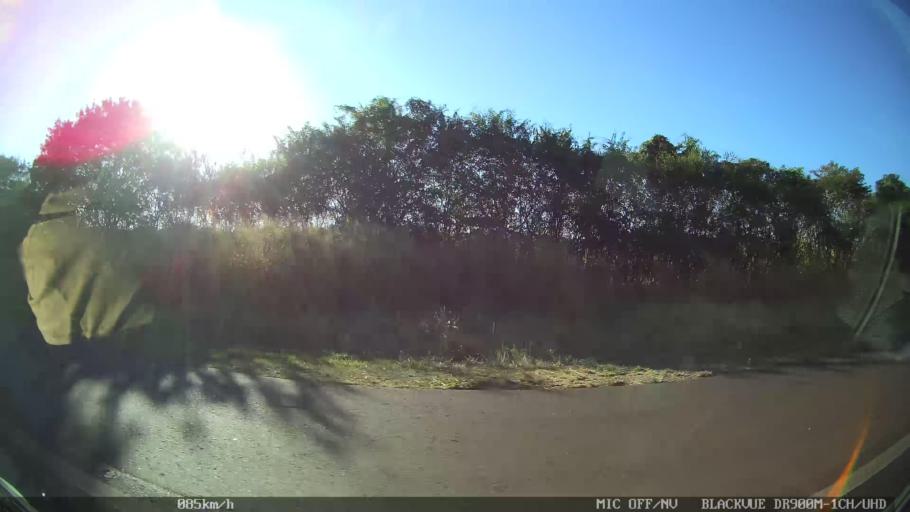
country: BR
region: Sao Paulo
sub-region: Guapiacu
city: Guapiacu
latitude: -20.7541
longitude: -49.1498
